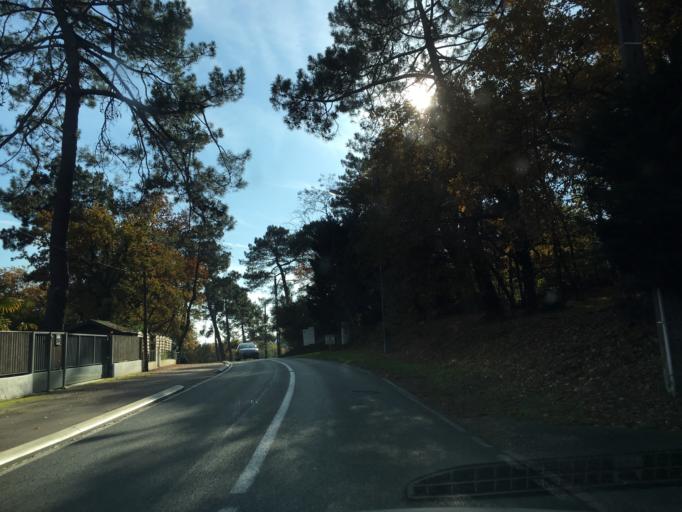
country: FR
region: Aquitaine
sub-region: Departement de la Gironde
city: Arcachon
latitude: 44.6381
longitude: -1.1719
